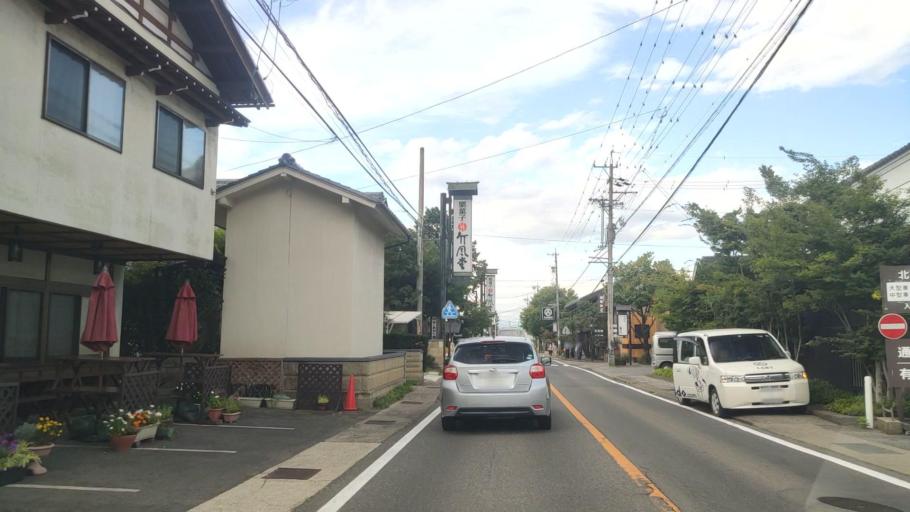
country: JP
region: Nagano
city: Suzaka
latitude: 36.6945
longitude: 138.3157
